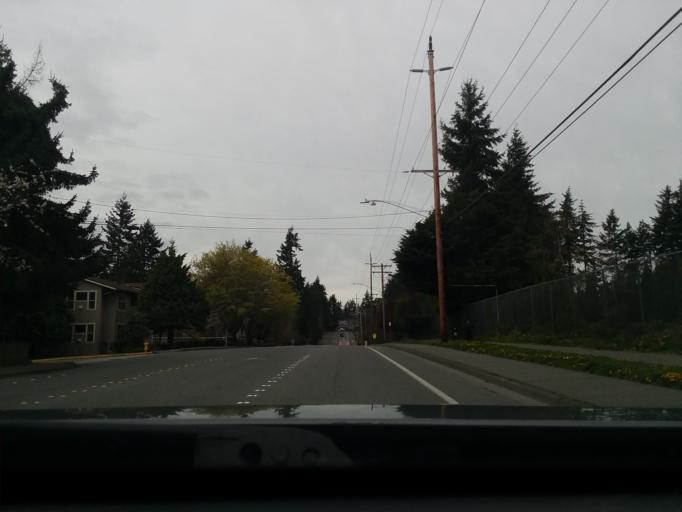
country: US
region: Washington
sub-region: Snohomish County
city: Lynnwood
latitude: 47.8106
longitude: -122.3298
